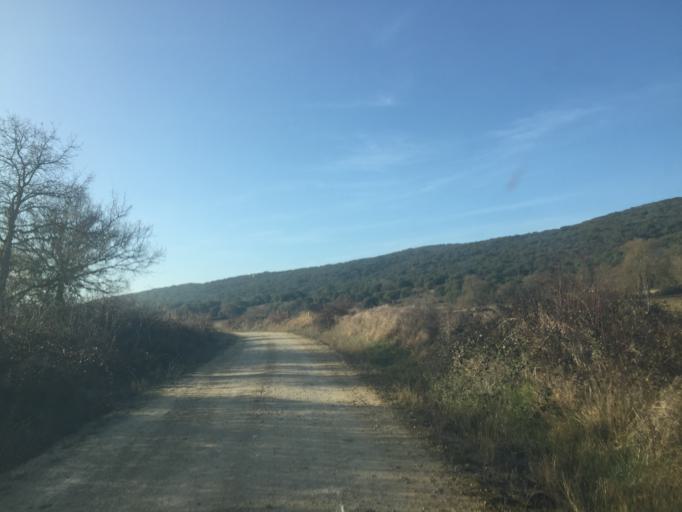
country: ES
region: Castille and Leon
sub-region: Provincia de Burgos
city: Medina de Pomar
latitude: 42.9279
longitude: -3.5937
